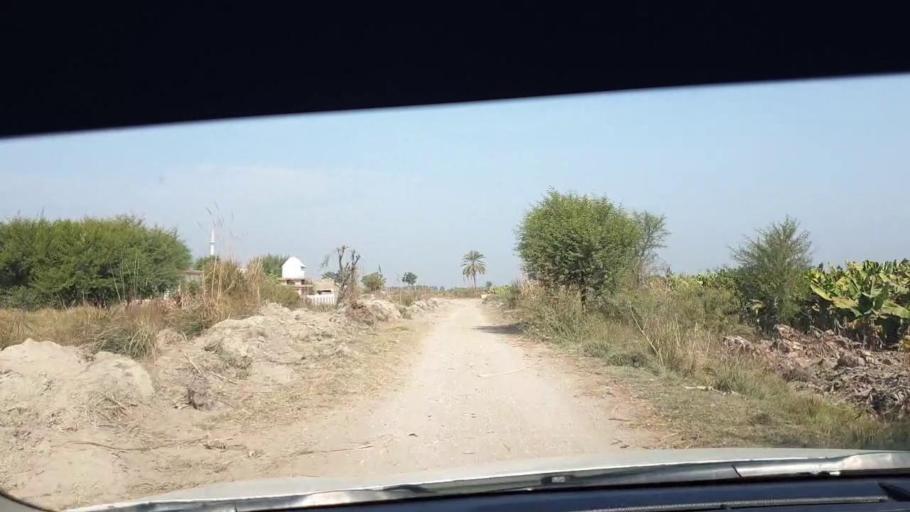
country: PK
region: Sindh
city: Tando Adam
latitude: 25.7394
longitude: 68.7026
